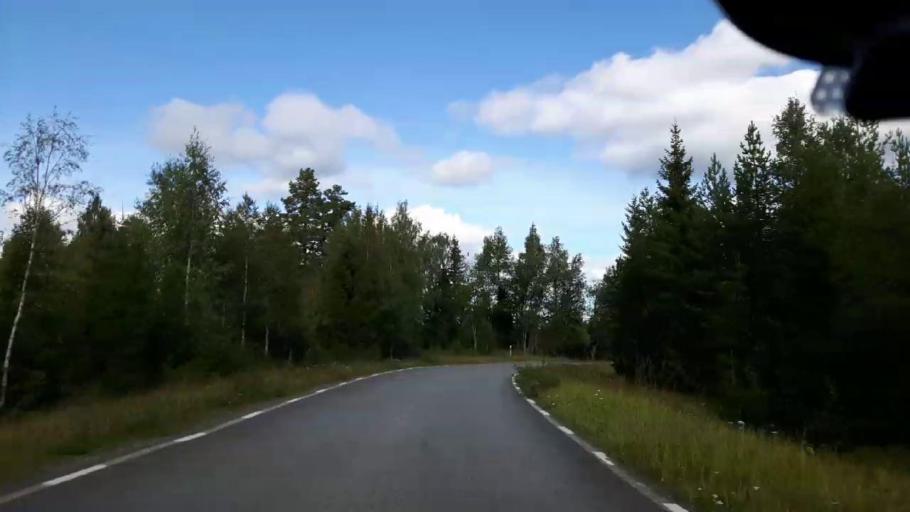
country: SE
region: Jaemtland
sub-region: OEstersunds Kommun
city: Brunflo
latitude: 63.2188
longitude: 15.2441
